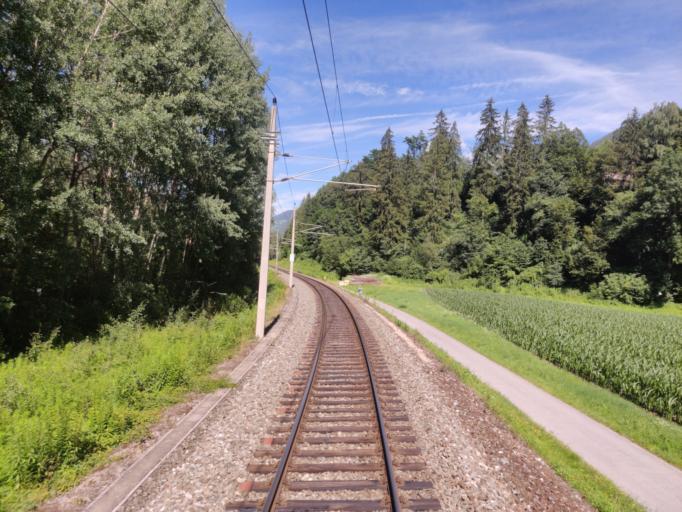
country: AT
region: Tyrol
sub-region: Politischer Bezirk Imst
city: Karres
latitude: 47.2105
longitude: 10.7985
